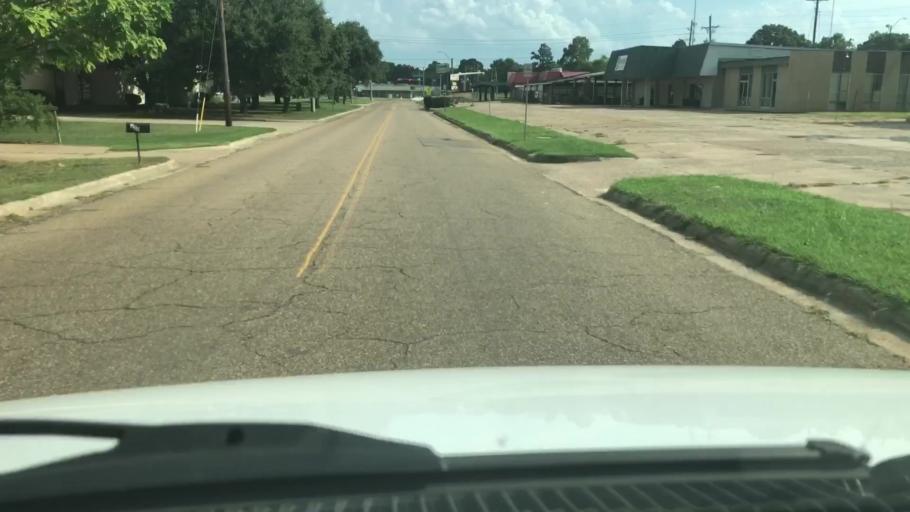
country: US
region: Texas
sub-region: Bowie County
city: Wake Village
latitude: 33.4390
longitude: -94.0826
